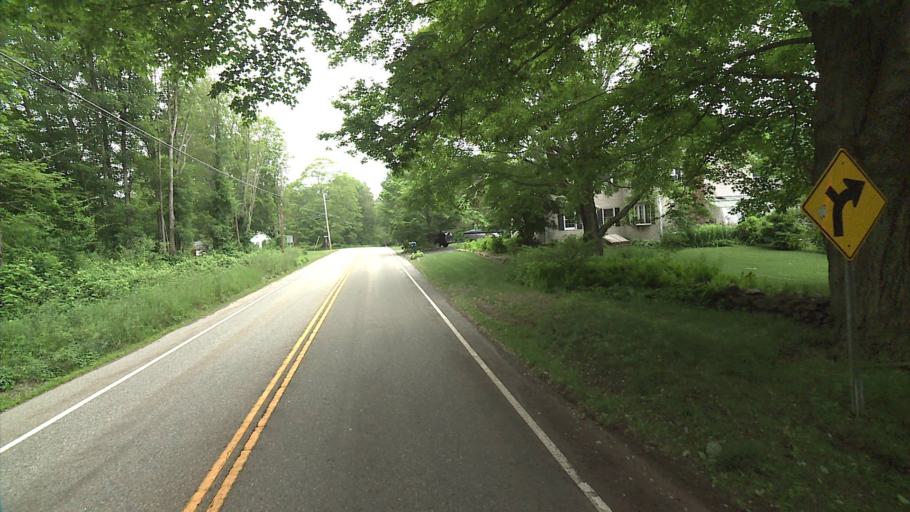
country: US
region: Connecticut
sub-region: Tolland County
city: Hebron
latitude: 41.7197
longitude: -72.3713
